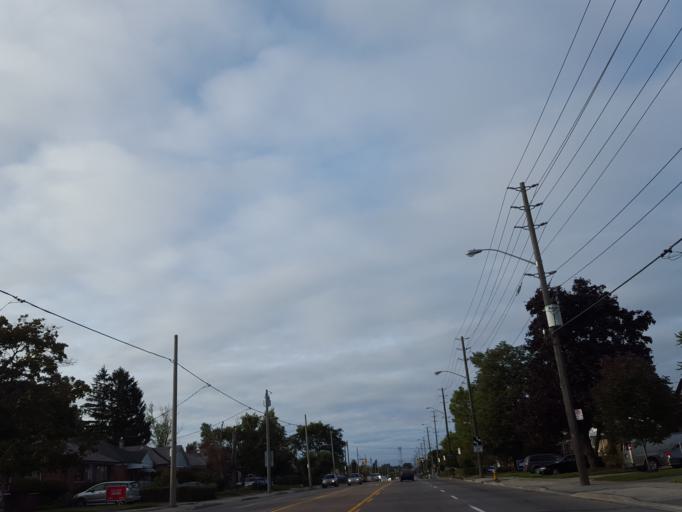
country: CA
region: Ontario
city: Scarborough
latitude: 43.7526
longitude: -79.2976
